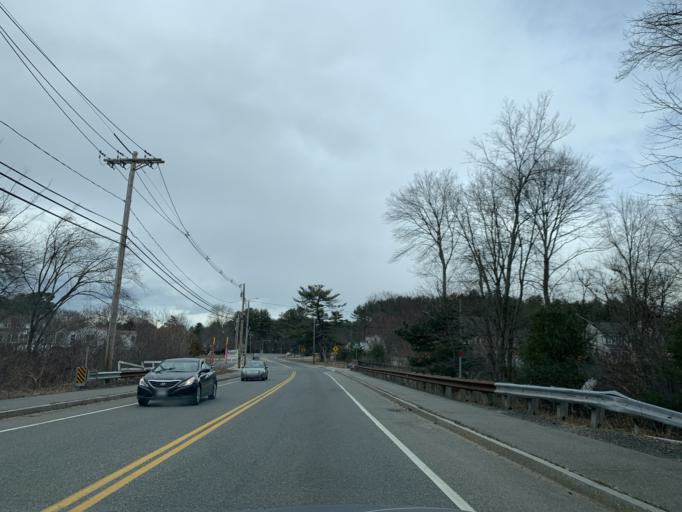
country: US
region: Rhode Island
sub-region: Providence County
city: Woonsocket
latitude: 42.0349
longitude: -71.4821
